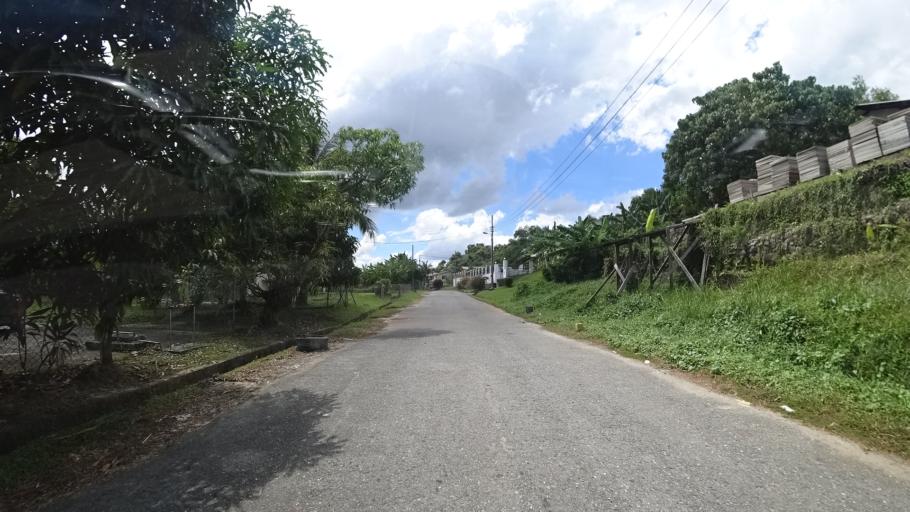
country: BN
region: Brunei and Muara
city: Bandar Seri Begawan
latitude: 4.8579
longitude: 114.8971
